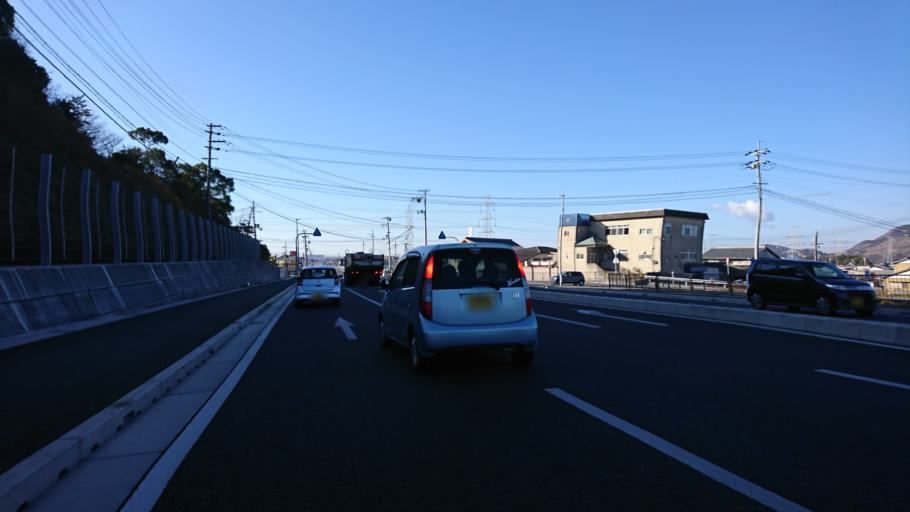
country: JP
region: Hyogo
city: Kakogawacho-honmachi
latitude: 34.8014
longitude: 134.8309
